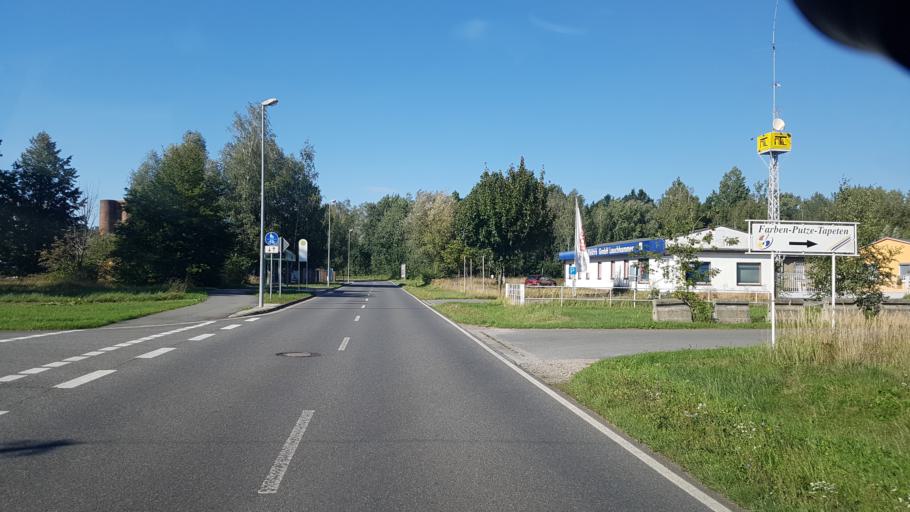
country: DE
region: Brandenburg
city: Lauchhammer
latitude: 51.4870
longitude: 13.7319
